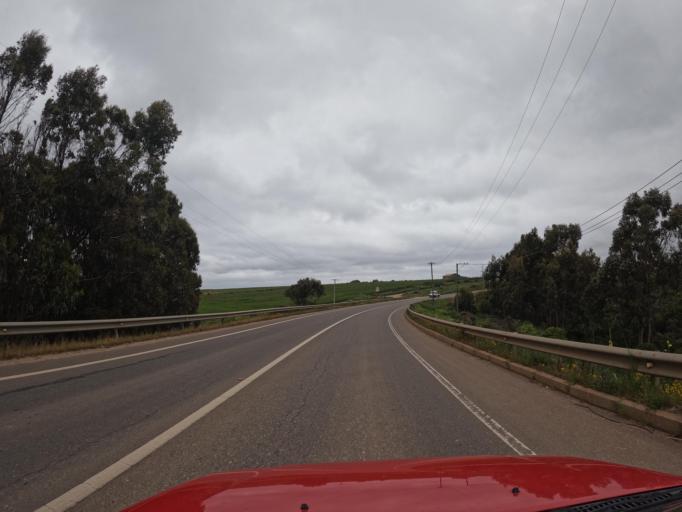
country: CL
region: O'Higgins
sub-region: Provincia de Colchagua
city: Santa Cruz
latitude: -34.4893
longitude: -72.0187
